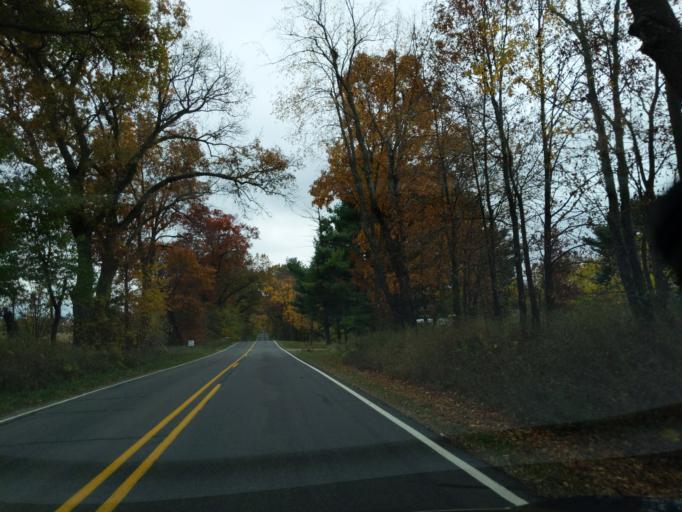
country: US
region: Michigan
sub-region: Eaton County
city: Eaton Rapids
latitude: 42.3847
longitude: -84.6005
